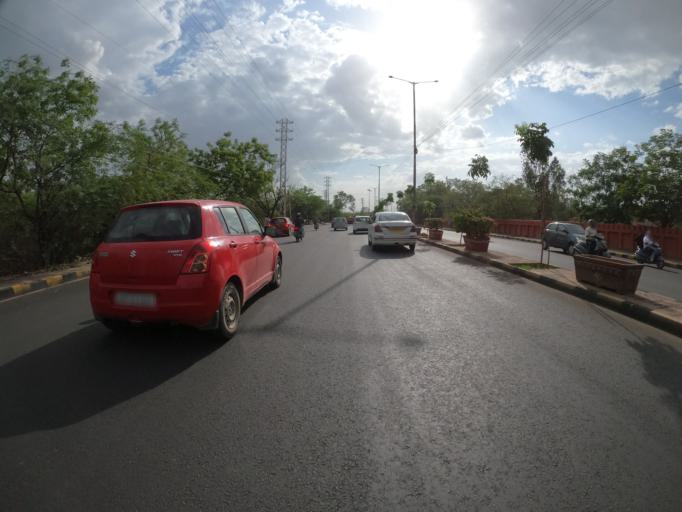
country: IN
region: Telangana
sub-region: Hyderabad
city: Hyderabad
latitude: 17.3730
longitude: 78.4072
